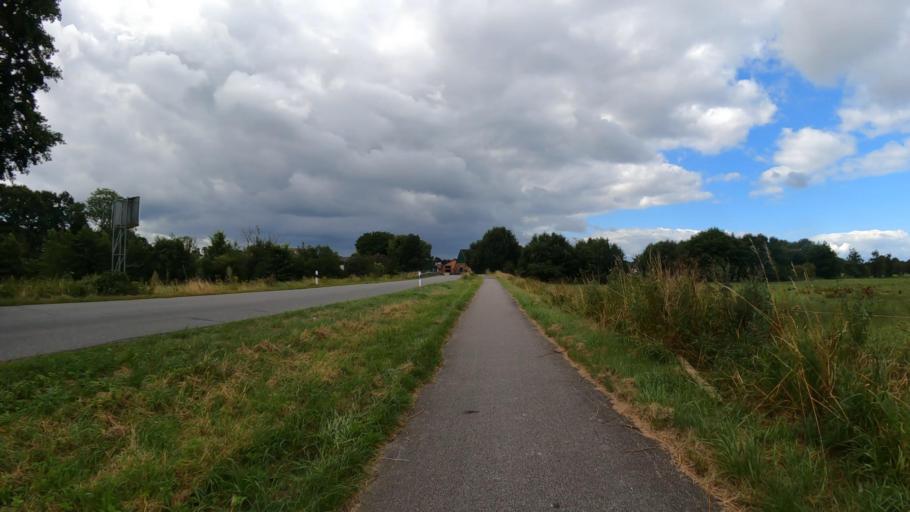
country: DE
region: Schleswig-Holstein
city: Padenstedt
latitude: 54.0519
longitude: 9.9176
